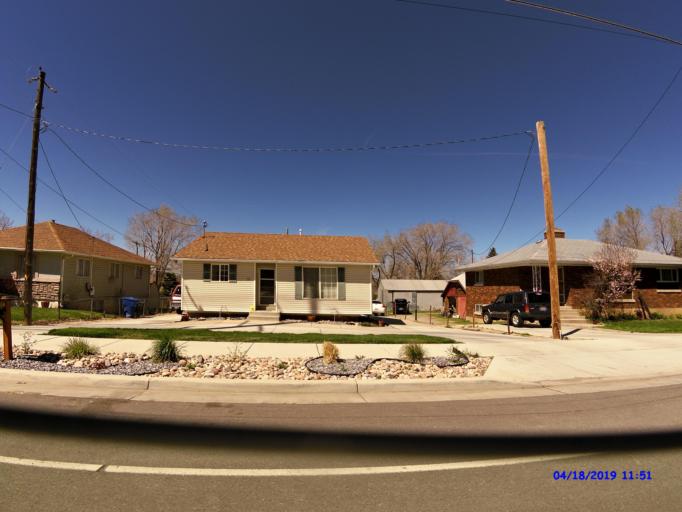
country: US
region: Utah
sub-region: Weber County
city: Ogden
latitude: 41.2534
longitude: -111.9480
